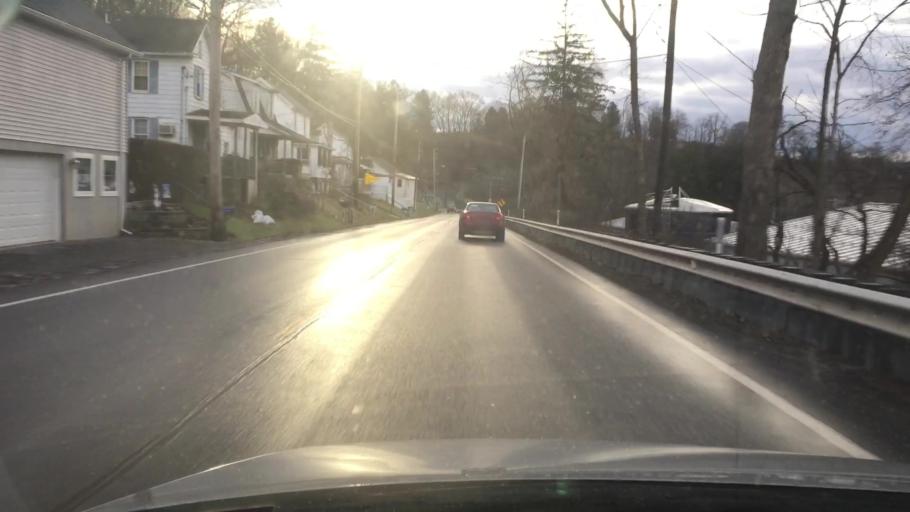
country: US
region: Pennsylvania
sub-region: Columbia County
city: Bloomsburg
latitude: 41.0082
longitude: -76.4624
